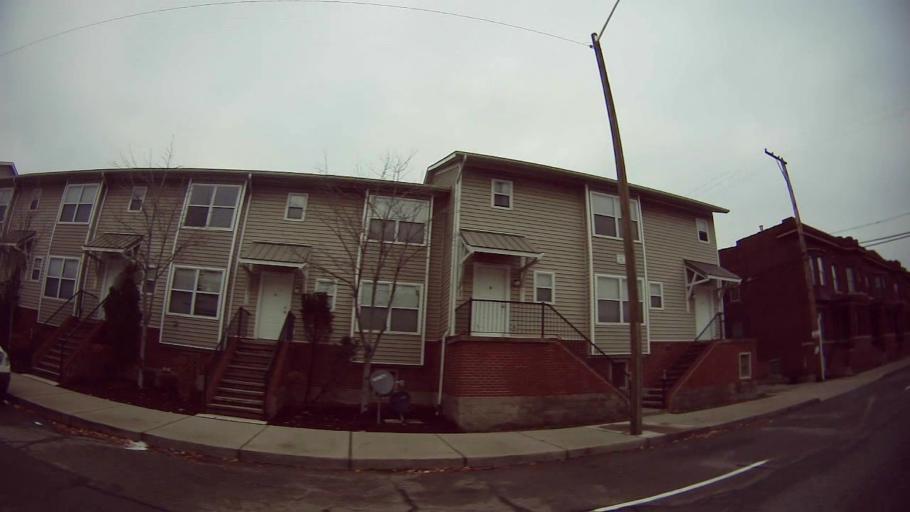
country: US
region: Michigan
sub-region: Wayne County
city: Hamtramck
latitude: 42.3657
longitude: -83.0675
